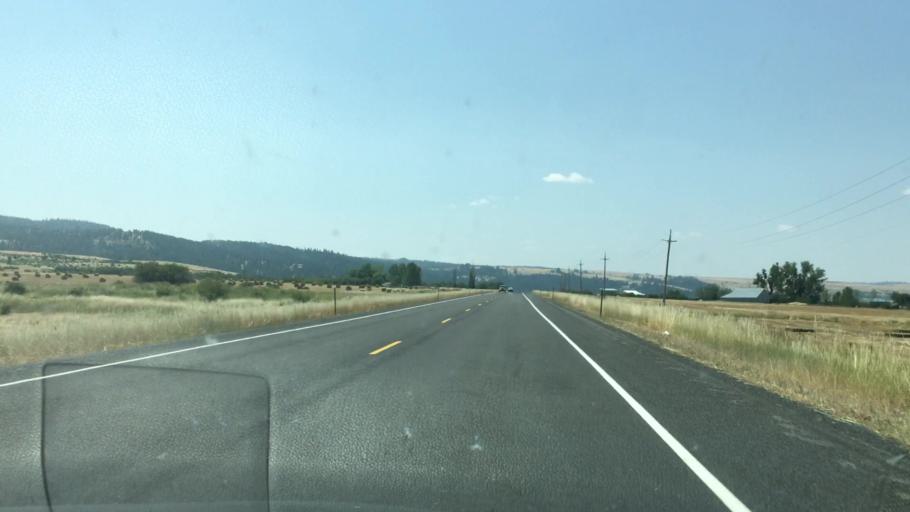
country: US
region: Idaho
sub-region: Idaho County
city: Grangeville
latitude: 45.9016
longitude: -116.1784
